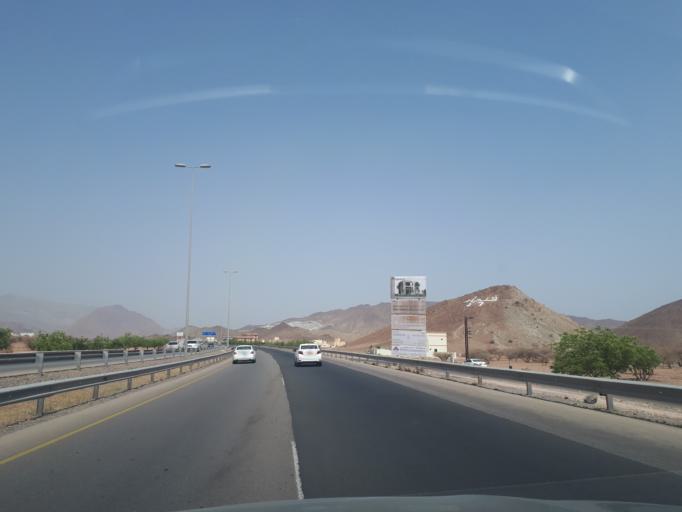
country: OM
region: Muhafazat ad Dakhiliyah
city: Bidbid
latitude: 23.4667
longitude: 58.1460
